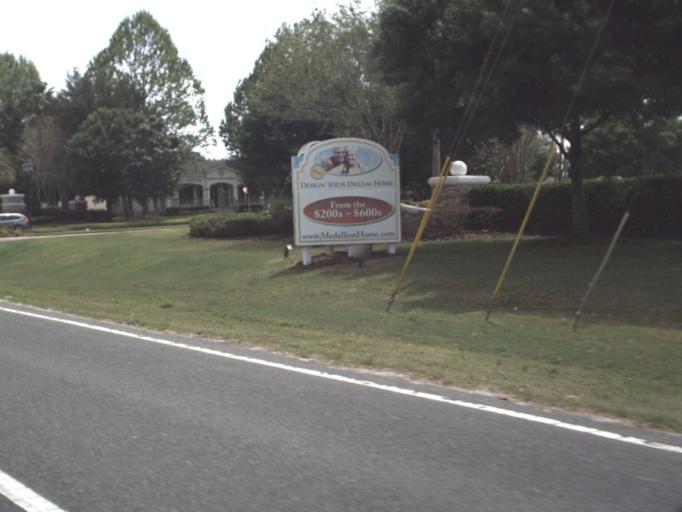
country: US
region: Florida
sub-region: Lake County
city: Mount Dora
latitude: 28.8516
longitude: -81.6211
